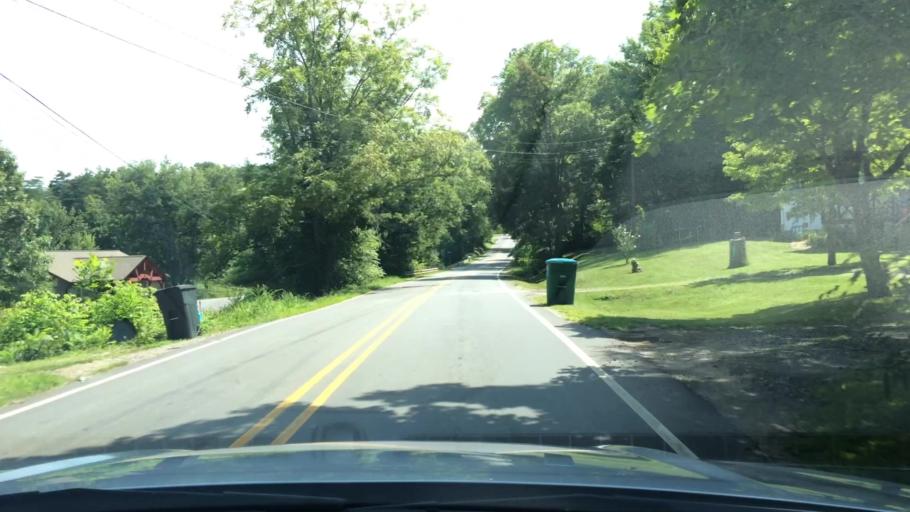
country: US
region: North Carolina
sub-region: Buncombe County
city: Weaverville
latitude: 35.6825
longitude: -82.5865
